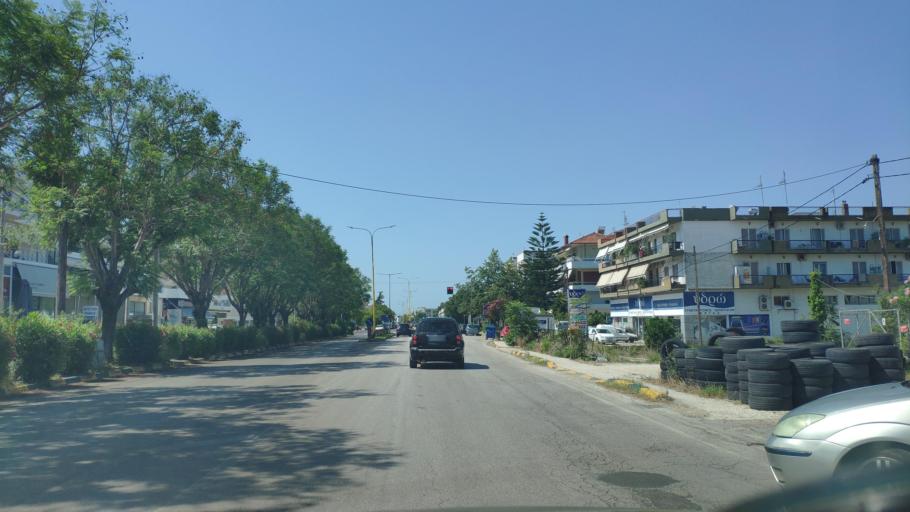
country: GR
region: Epirus
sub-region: Nomos Artas
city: Arta
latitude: 39.1583
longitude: 20.9797
